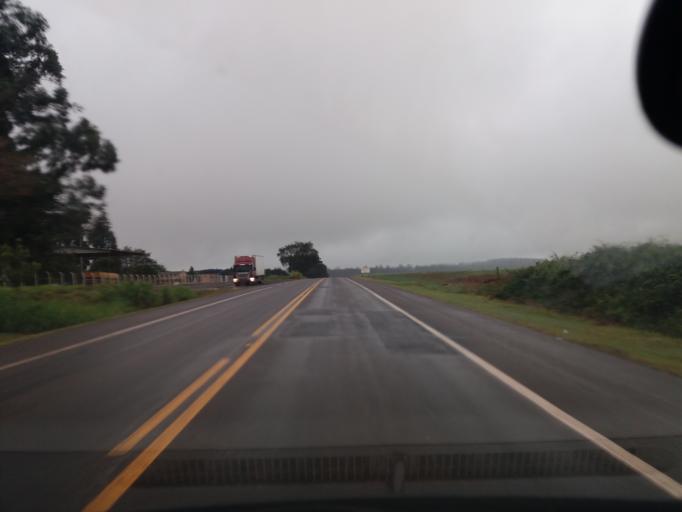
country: BR
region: Parana
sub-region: Campo Mourao
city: Campo Mourao
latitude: -24.2980
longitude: -52.5867
